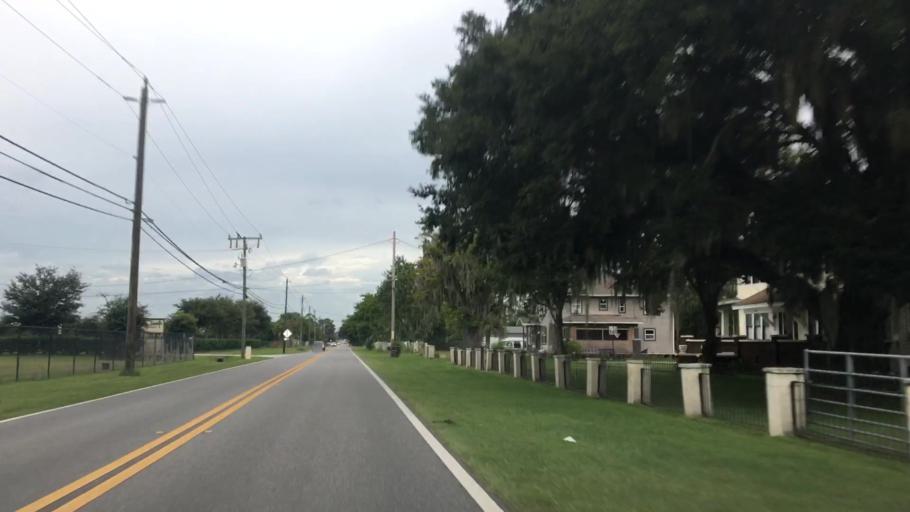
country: US
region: Florida
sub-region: Seminole County
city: Midway
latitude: 28.8014
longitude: -81.2326
